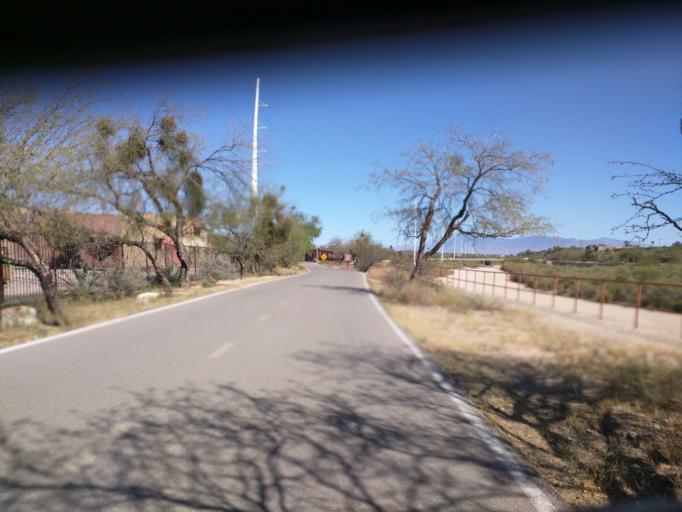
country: US
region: Arizona
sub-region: Pima County
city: Flowing Wells
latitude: 32.2901
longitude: -110.9663
